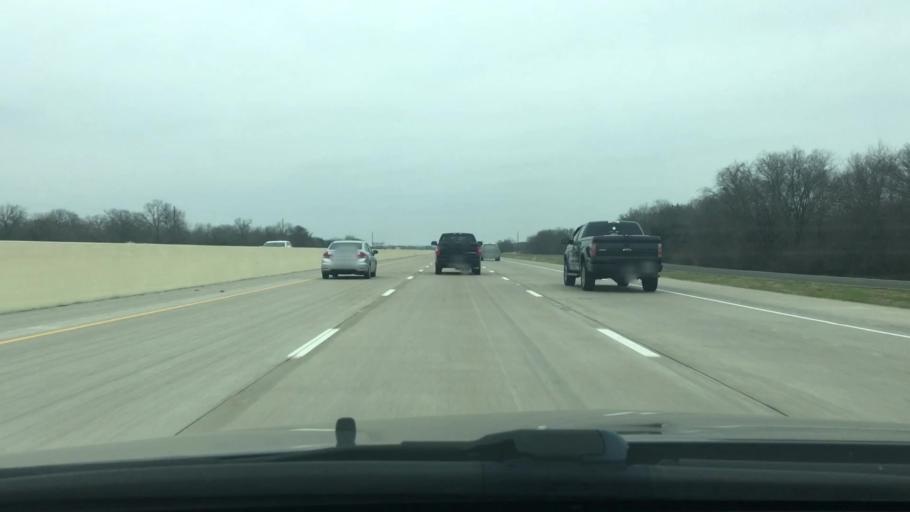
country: US
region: Texas
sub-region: Navarro County
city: Corsicana
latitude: 31.9793
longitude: -96.4237
